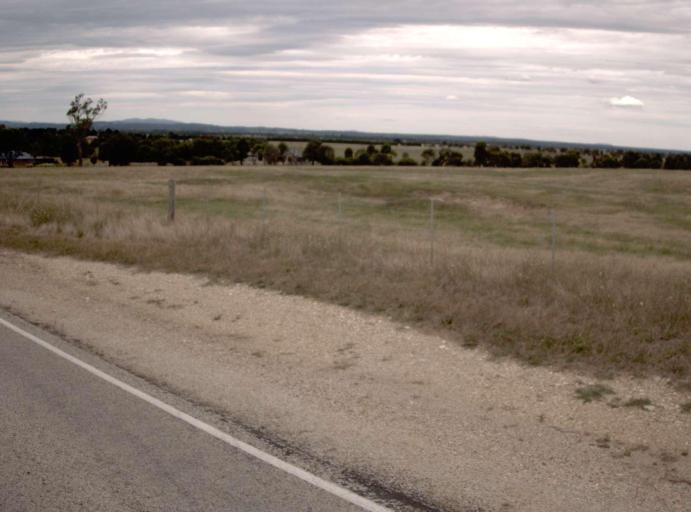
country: AU
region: Victoria
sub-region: East Gippsland
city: Bairnsdale
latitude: -37.8725
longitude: 147.5608
